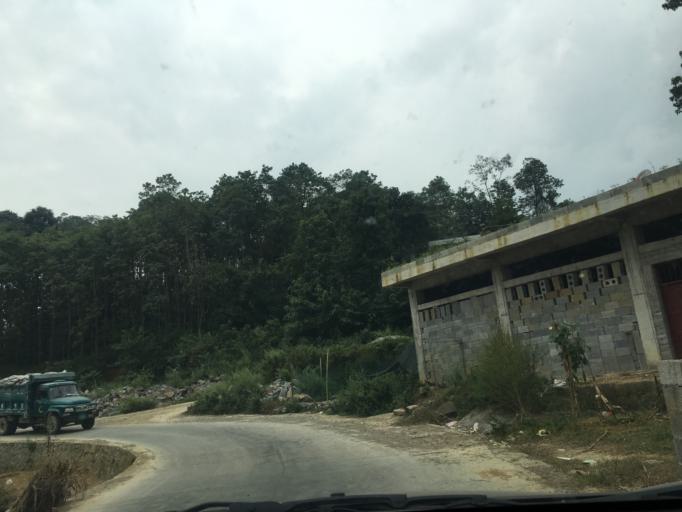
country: CN
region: Guangxi Zhuangzu Zizhiqu
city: Xinzhou
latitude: 25.5364
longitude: 105.6118
